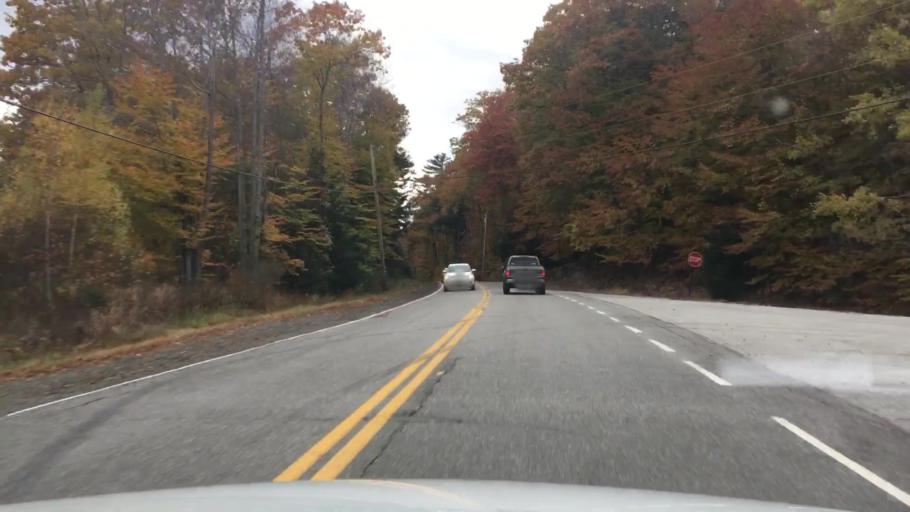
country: US
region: Maine
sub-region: Androscoggin County
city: Sabattus
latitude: 44.1309
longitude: -70.0407
